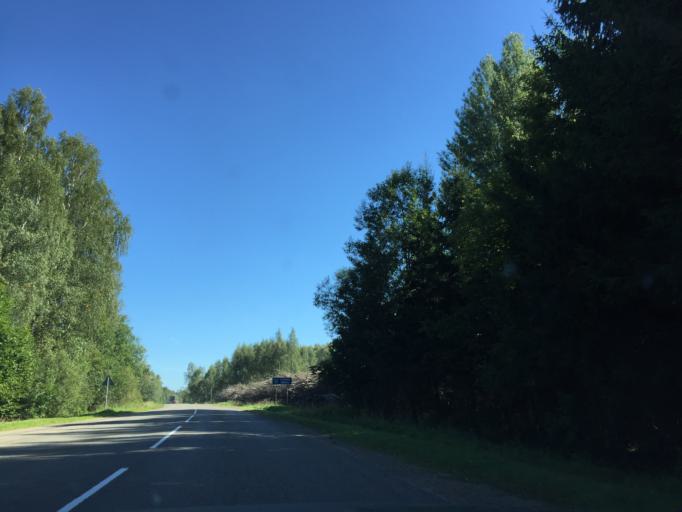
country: LV
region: Akniste
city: Akniste
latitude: 56.1135
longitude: 25.8388
